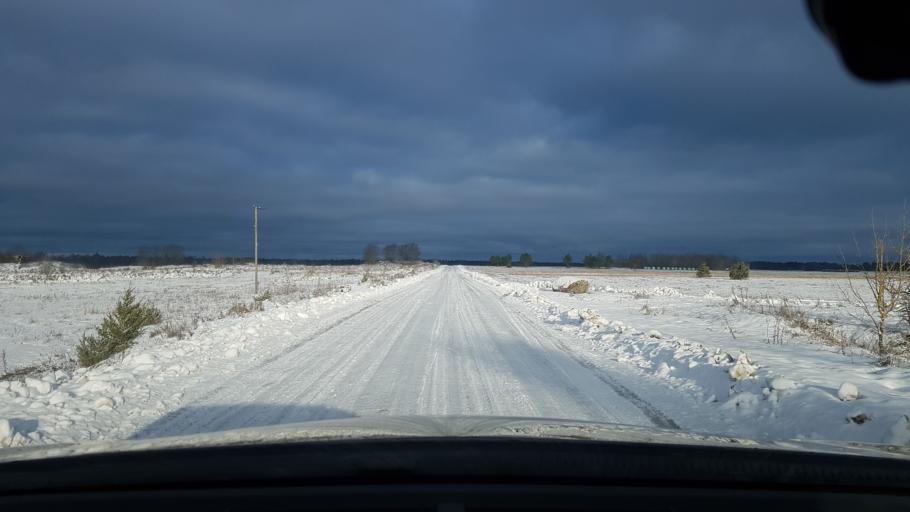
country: EE
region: Harju
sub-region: Keila linn
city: Keila
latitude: 59.3089
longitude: 24.2493
